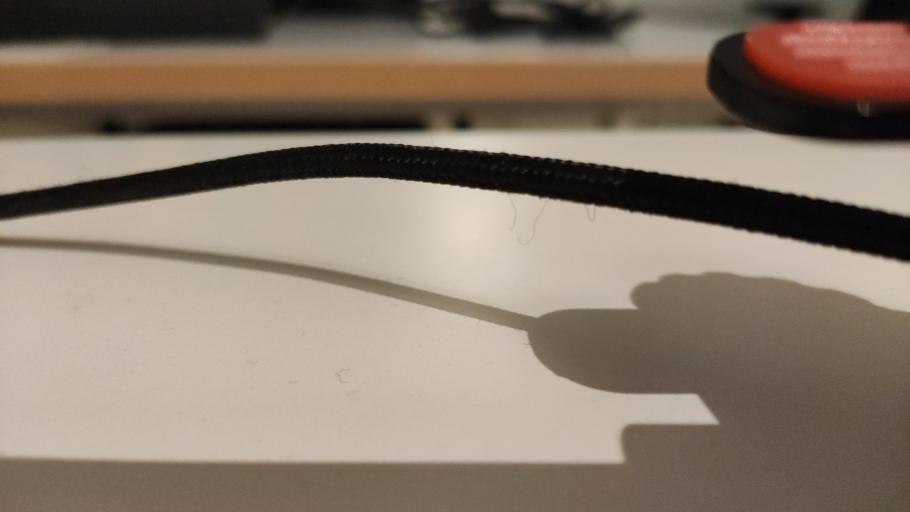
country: RU
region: Moskovskaya
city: Novosin'kovo
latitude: 56.3952
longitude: 37.2776
